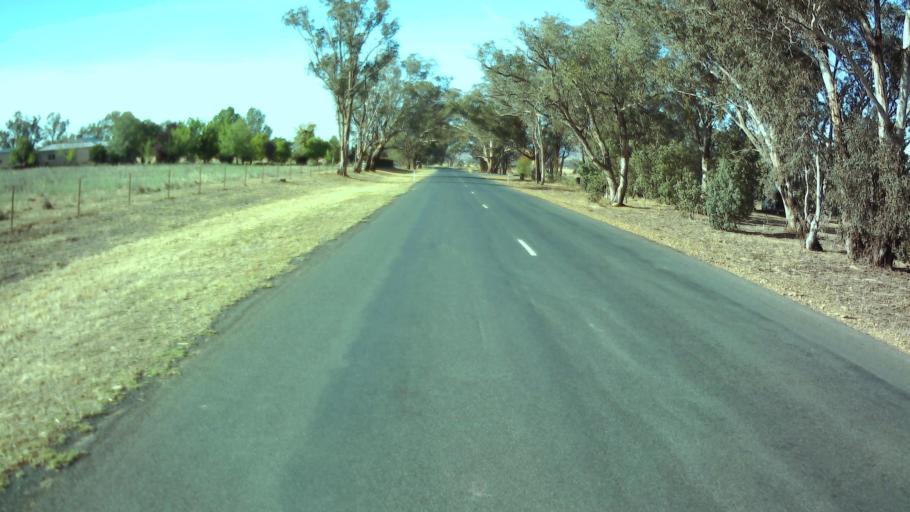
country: AU
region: New South Wales
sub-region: Weddin
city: Grenfell
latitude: -33.9131
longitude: 148.1436
